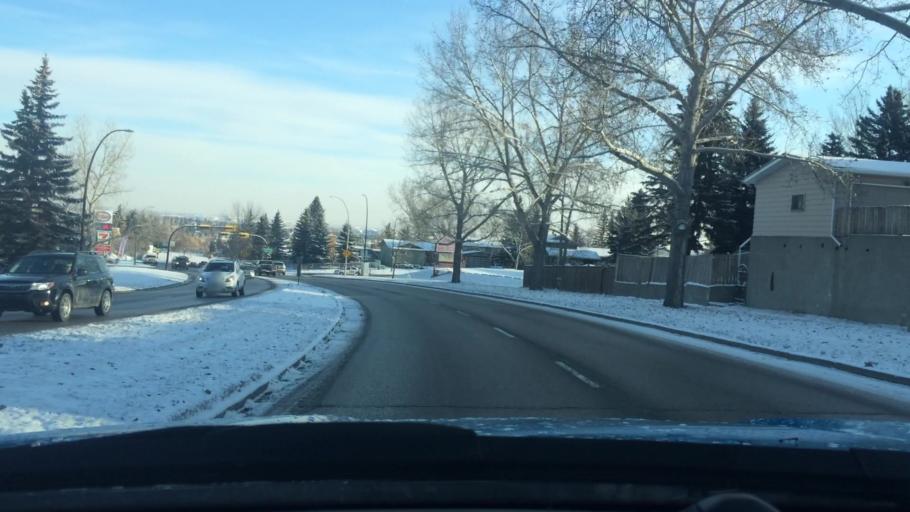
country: CA
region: Alberta
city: Calgary
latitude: 51.1094
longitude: -114.0792
